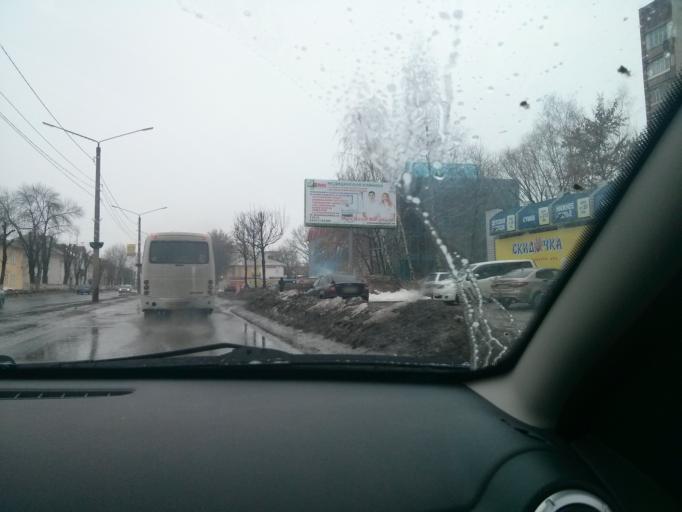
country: RU
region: Vladimir
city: Murom
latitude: 55.5762
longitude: 42.0354
